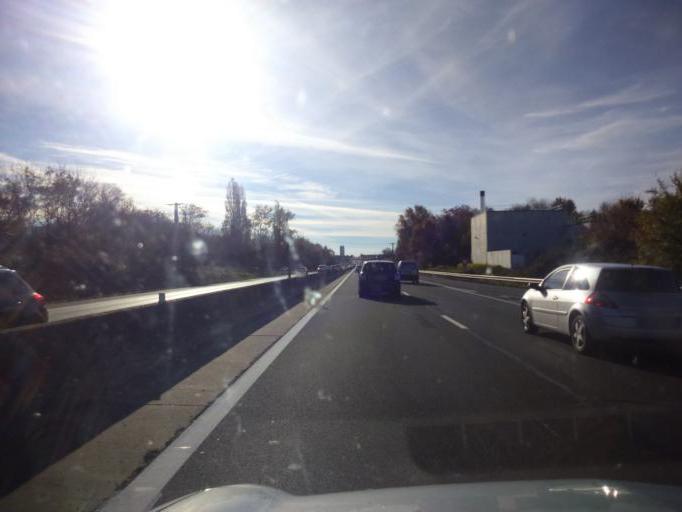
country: FR
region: Poitou-Charentes
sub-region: Departement de la Charente-Maritime
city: Perigny
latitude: 46.1519
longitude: -1.1131
